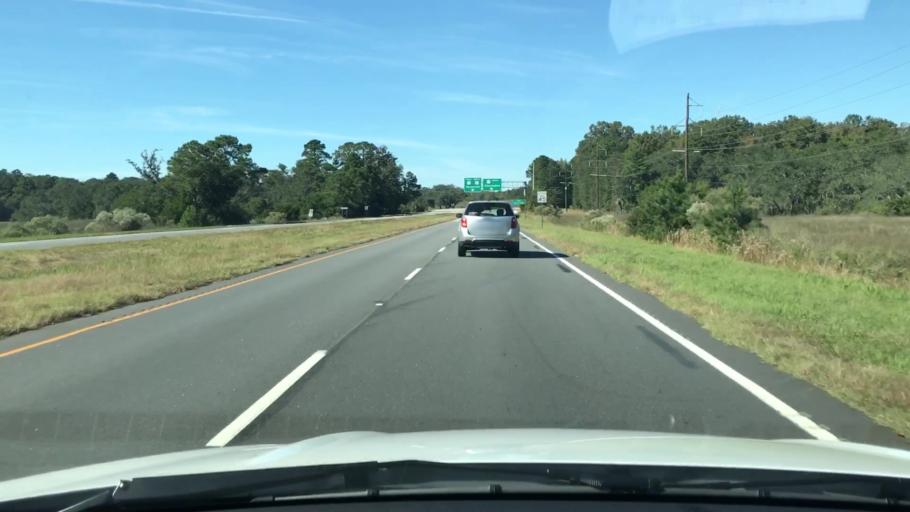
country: US
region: South Carolina
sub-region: Hampton County
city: Yemassee
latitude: 32.5971
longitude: -80.7553
